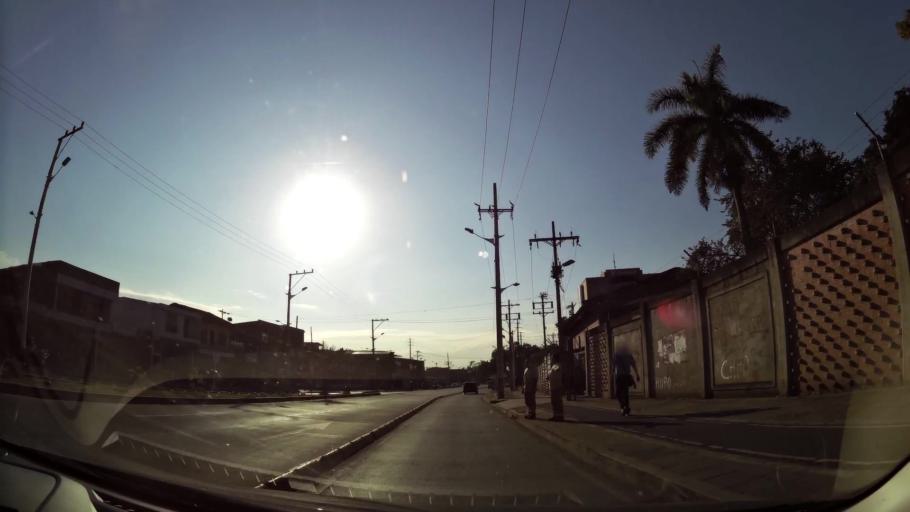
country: CO
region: Valle del Cauca
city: Cali
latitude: 3.4370
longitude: -76.5173
